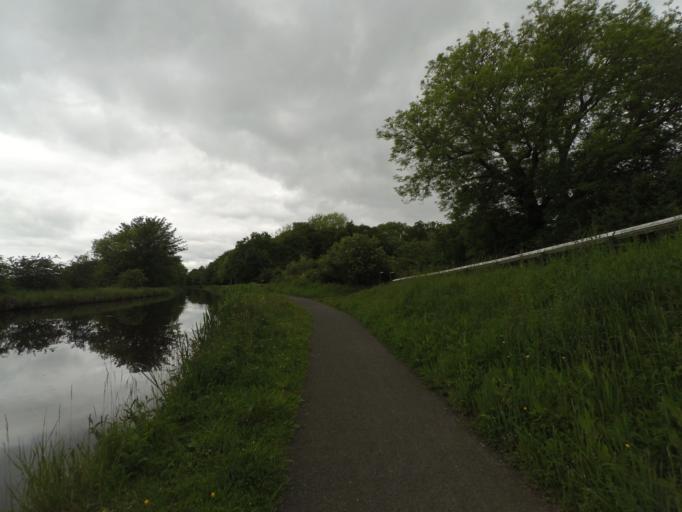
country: GB
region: Scotland
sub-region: West Lothian
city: Broxburn
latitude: 55.9650
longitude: -3.4643
